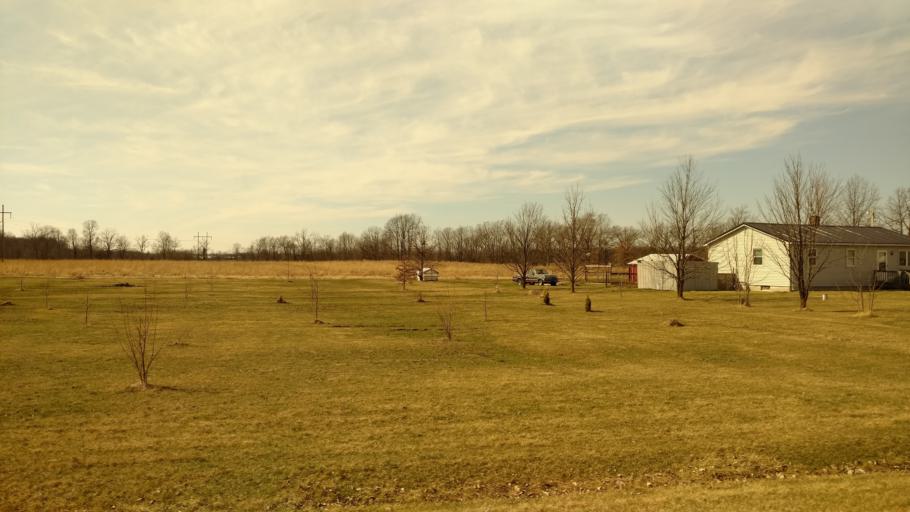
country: US
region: Ohio
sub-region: Hardin County
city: Kenton
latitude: 40.6023
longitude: -83.5037
